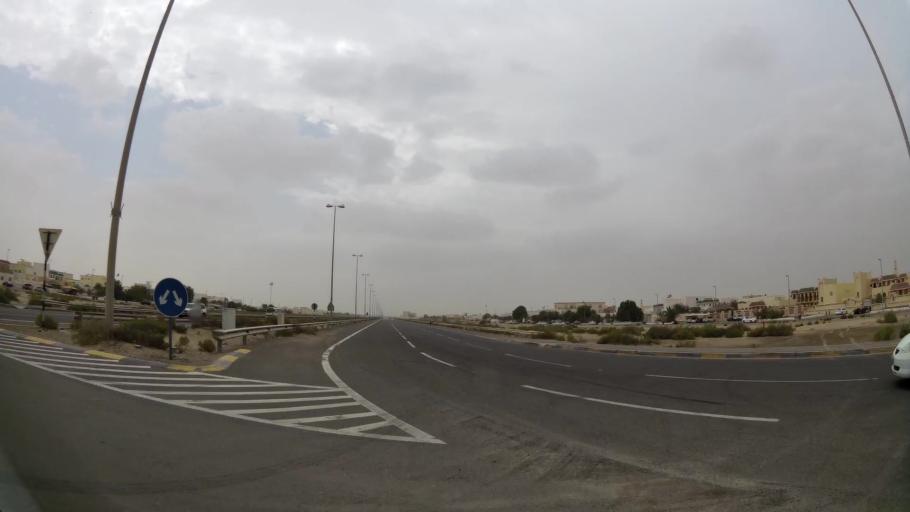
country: AE
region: Abu Dhabi
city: Abu Dhabi
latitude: 24.3783
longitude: 54.6671
